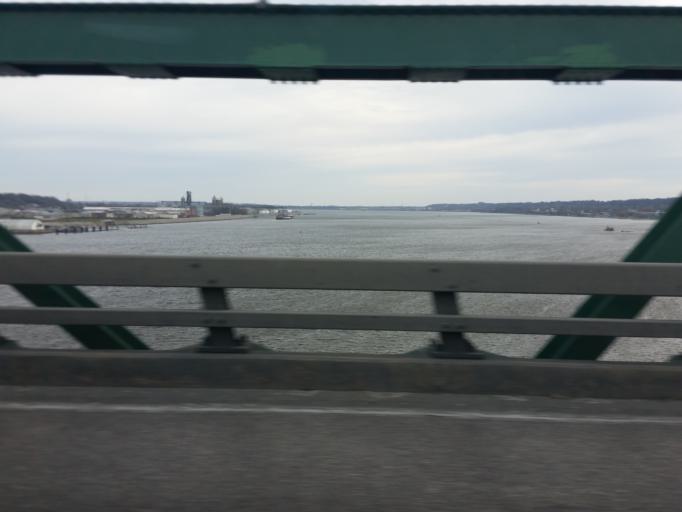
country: US
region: Iowa
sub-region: Scott County
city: Bettendorf
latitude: 41.5192
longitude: -90.5130
